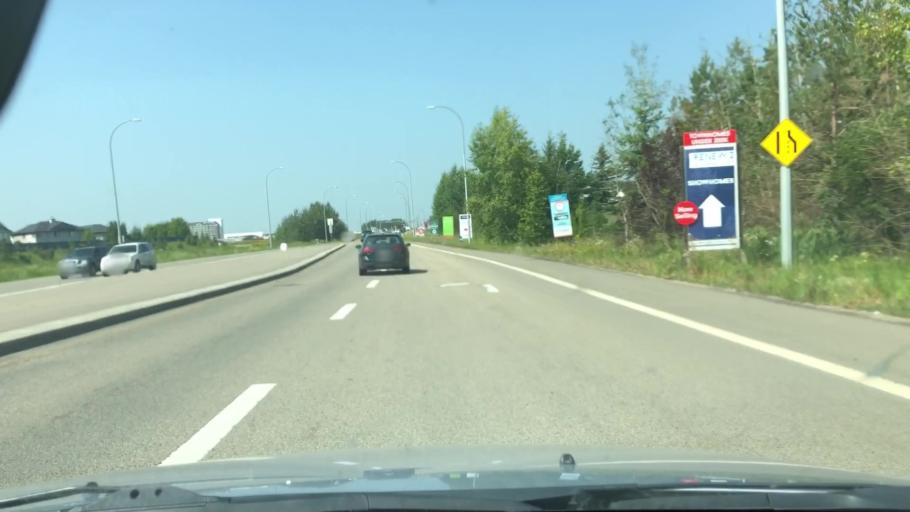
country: CA
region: Alberta
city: St. Albert
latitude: 53.5123
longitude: -113.6799
